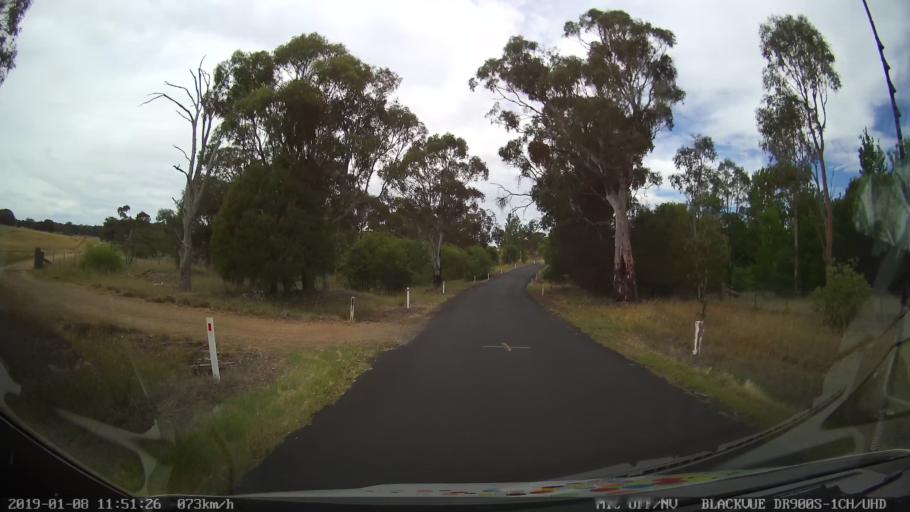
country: AU
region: New South Wales
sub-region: Armidale Dumaresq
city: Armidale
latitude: -30.3930
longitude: 151.5599
